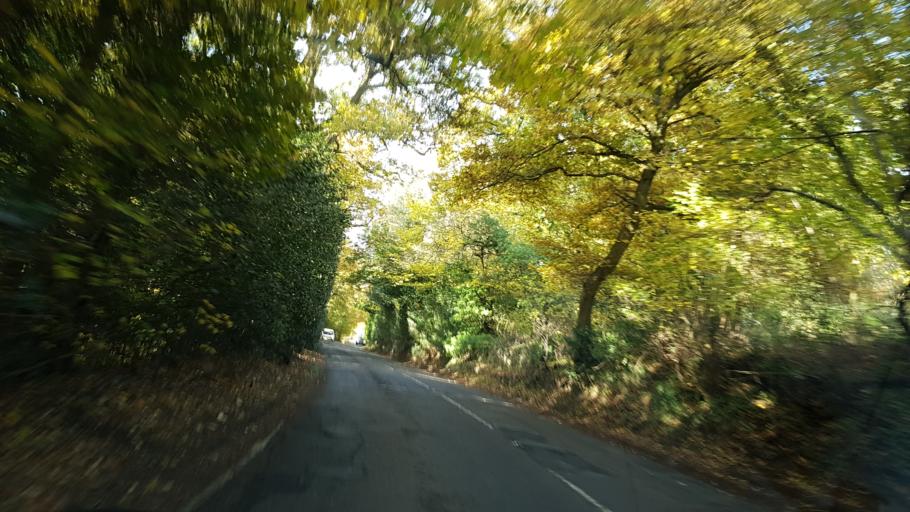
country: GB
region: England
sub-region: Surrey
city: Elstead
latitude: 51.1898
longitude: -0.7182
